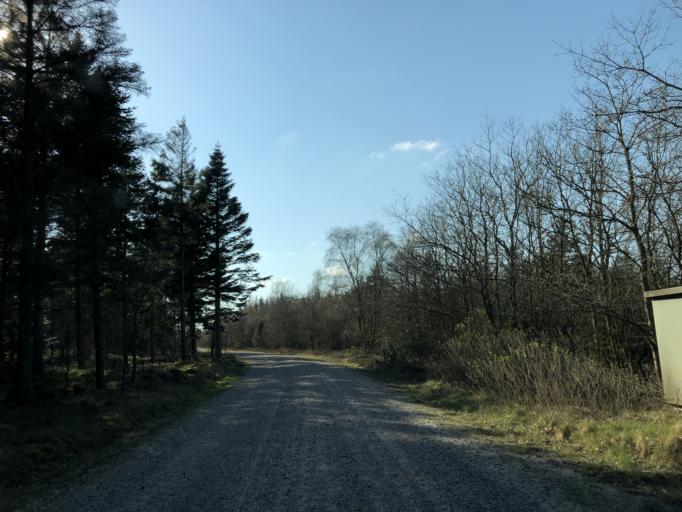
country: DK
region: Central Jutland
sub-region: Holstebro Kommune
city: Ulfborg
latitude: 56.3688
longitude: 8.2986
